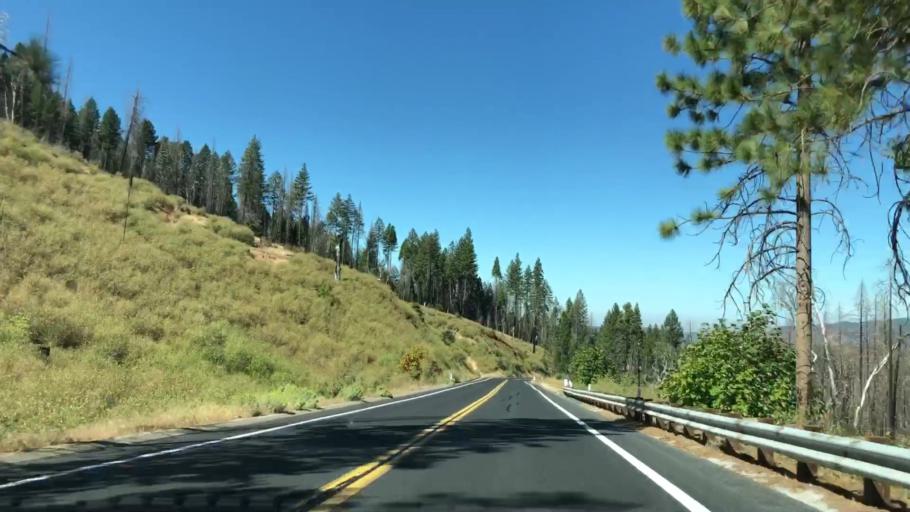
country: US
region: California
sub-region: Mariposa County
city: Midpines
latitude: 37.8274
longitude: -119.9760
